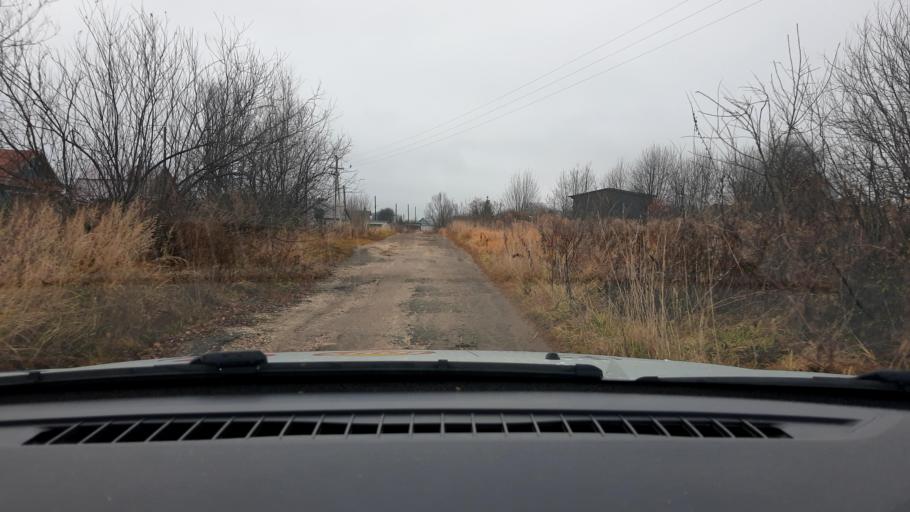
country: RU
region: Nizjnij Novgorod
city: Dal'neye Konstantinovo
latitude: 55.9616
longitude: 43.9818
